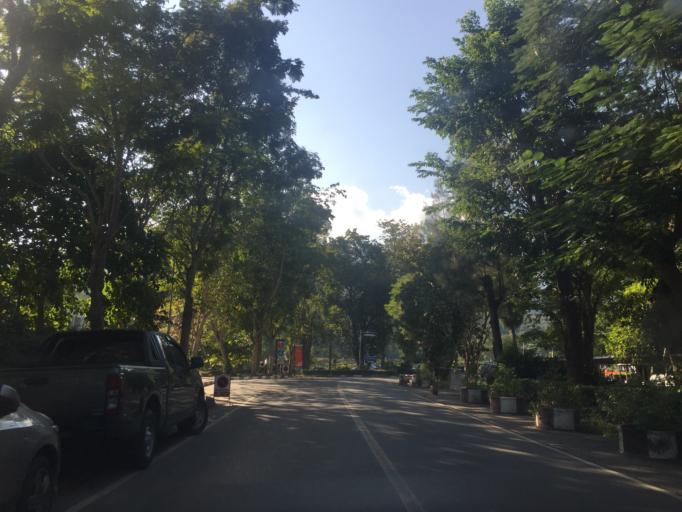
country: TH
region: Chiang Mai
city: Chiang Mai
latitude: 18.8032
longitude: 98.9501
